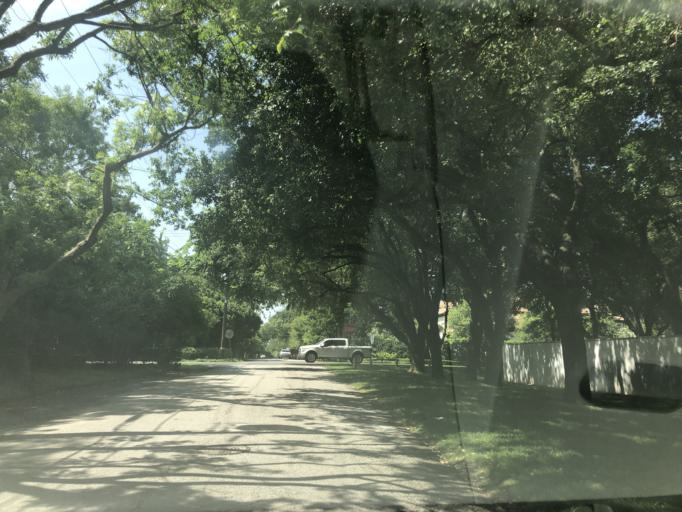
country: US
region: Texas
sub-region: Dallas County
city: University Park
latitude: 32.8745
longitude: -96.8175
